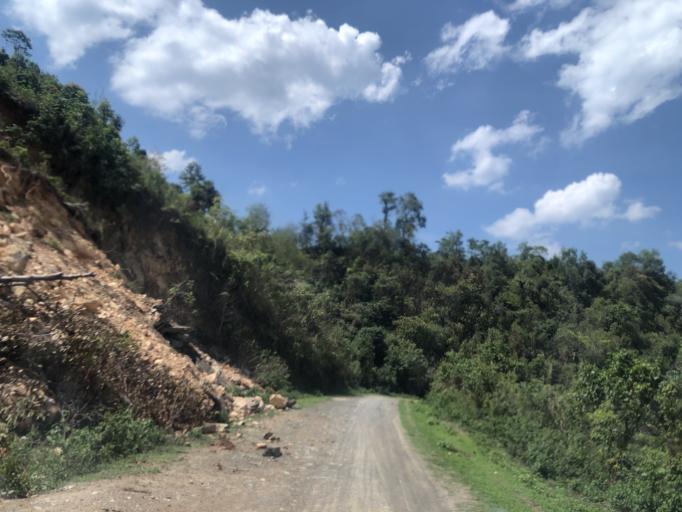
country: LA
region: Phongsali
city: Phongsali
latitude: 21.4196
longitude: 102.2510
